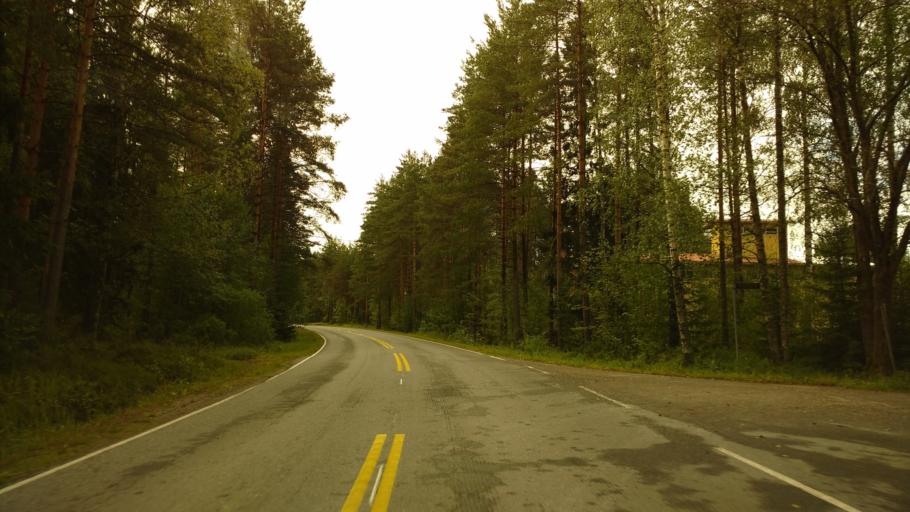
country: FI
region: Varsinais-Suomi
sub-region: Loimaa
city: Koski Tl
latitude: 60.6297
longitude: 23.1051
